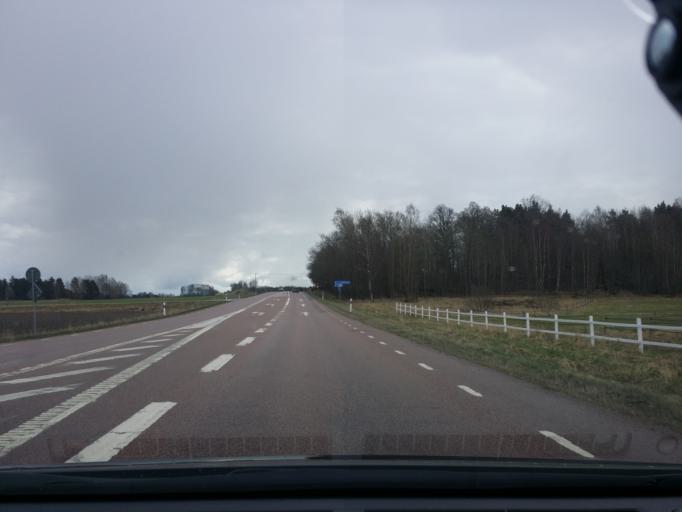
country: SE
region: Uppsala
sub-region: Enkopings Kommun
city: Enkoping
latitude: 59.6711
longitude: 17.0606
